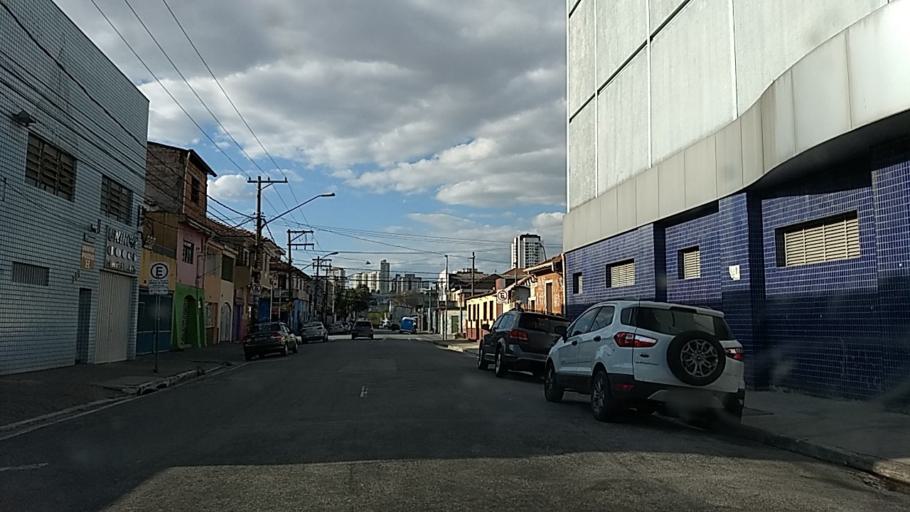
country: BR
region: Sao Paulo
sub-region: Sao Paulo
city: Sao Paulo
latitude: -23.5192
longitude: -46.5932
